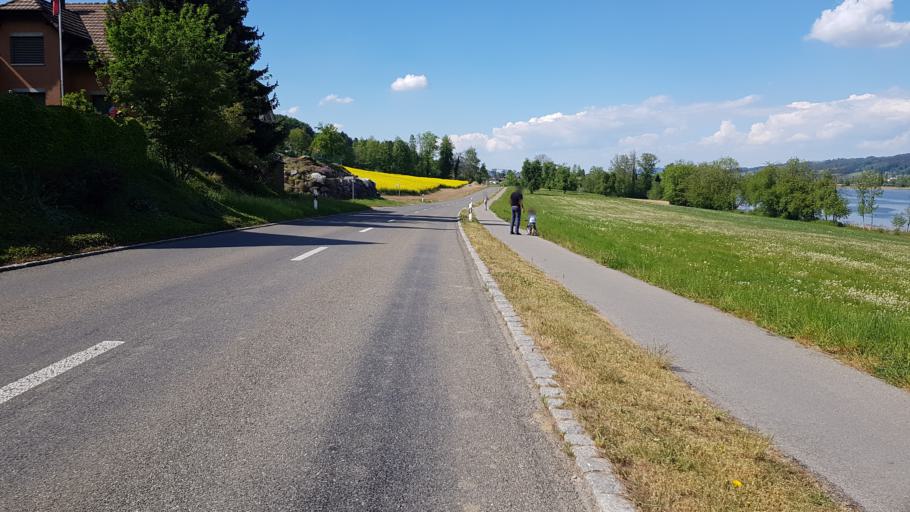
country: CH
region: Lucerne
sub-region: Hochdorf District
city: Hitzkirch
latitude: 47.2030
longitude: 8.2460
